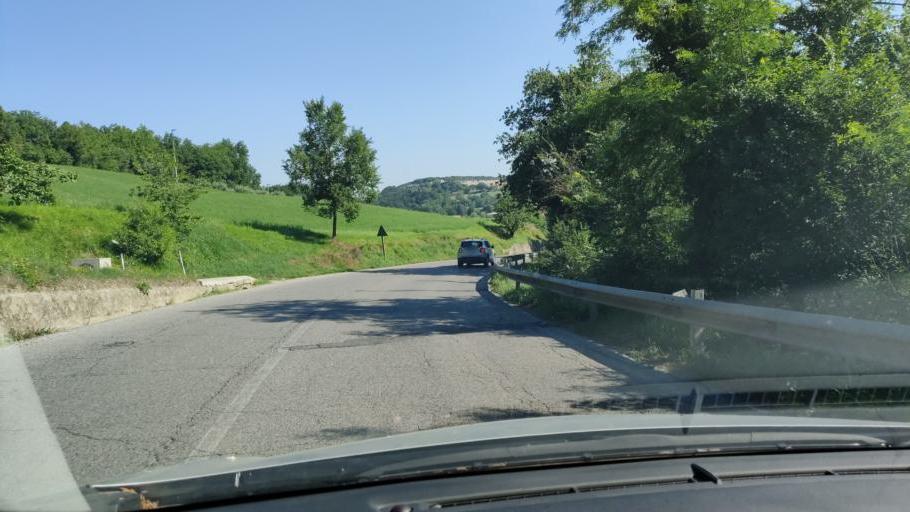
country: IT
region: Umbria
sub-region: Provincia di Perugia
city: Todi
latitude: 42.7873
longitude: 12.4165
